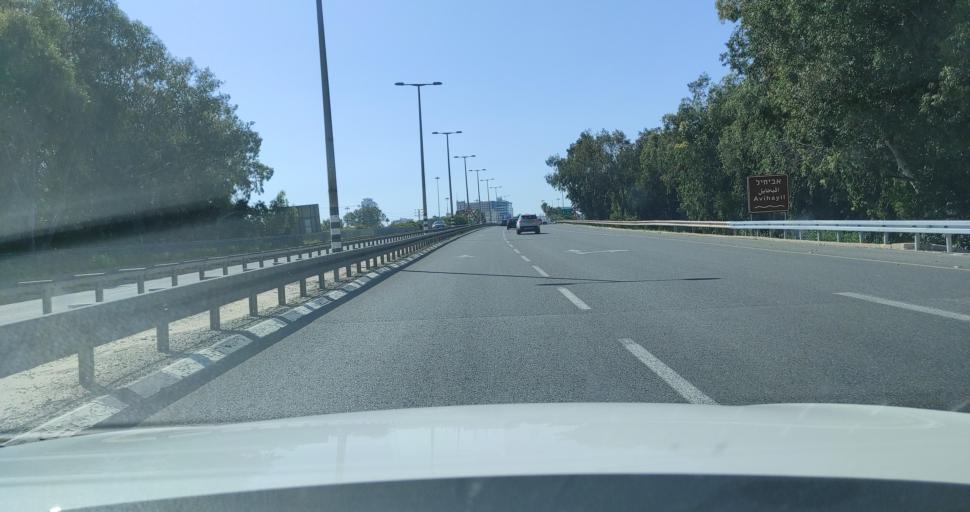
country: IL
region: Central District
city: Netanya
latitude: 32.3245
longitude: 34.8727
